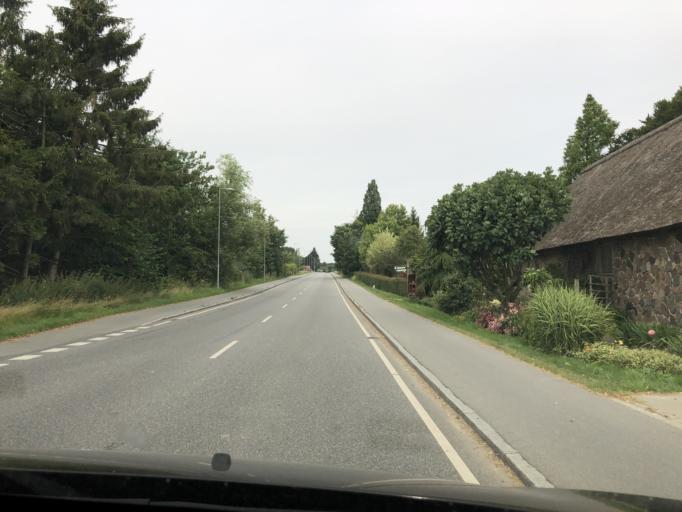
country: DK
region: South Denmark
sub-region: Assens Kommune
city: Glamsbjerg
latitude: 55.2571
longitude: 10.1325
